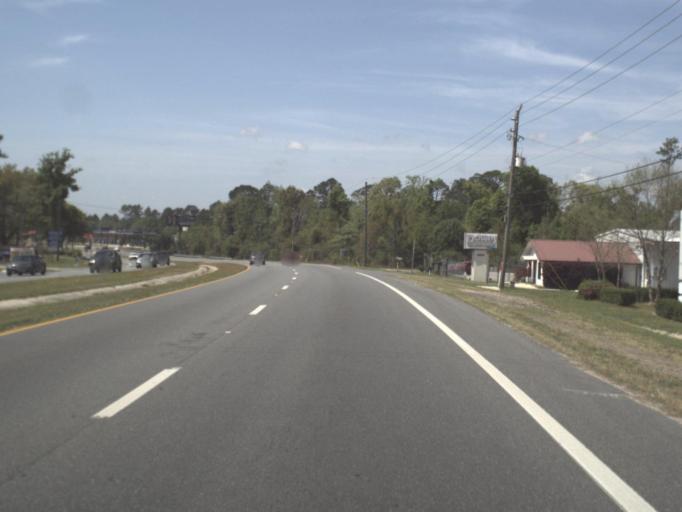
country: US
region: Florida
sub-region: Santa Rosa County
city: Pace
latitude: 30.5952
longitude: -87.1713
